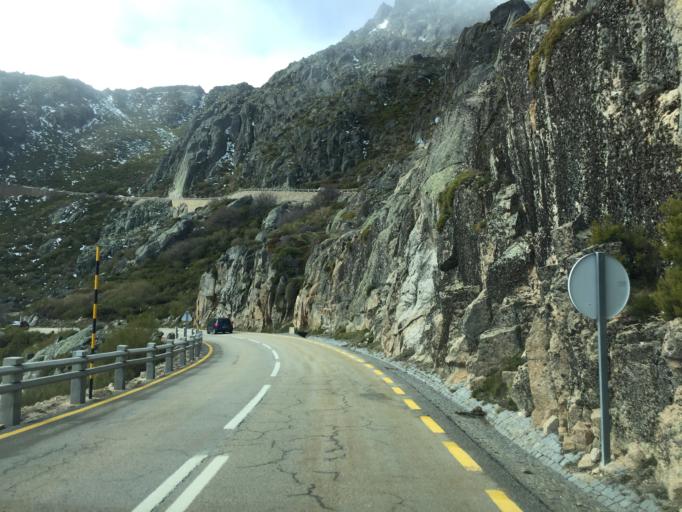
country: PT
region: Guarda
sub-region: Manteigas
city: Manteigas
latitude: 40.3240
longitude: -7.5899
